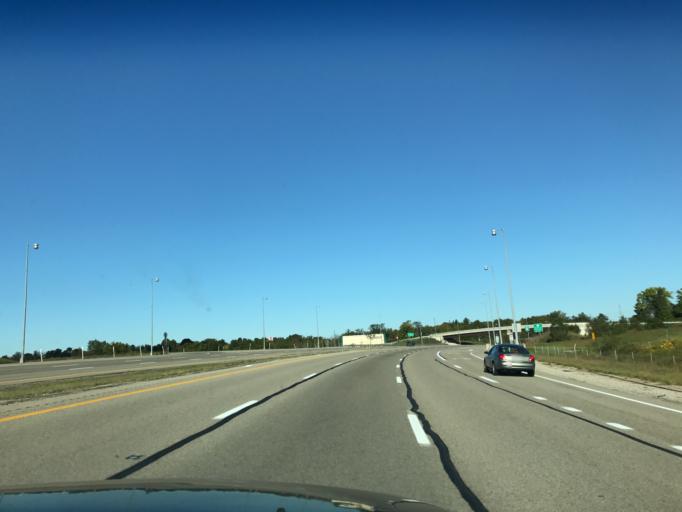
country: US
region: West Virginia
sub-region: Wood County
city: Blennerhassett
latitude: 39.2574
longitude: -81.6414
